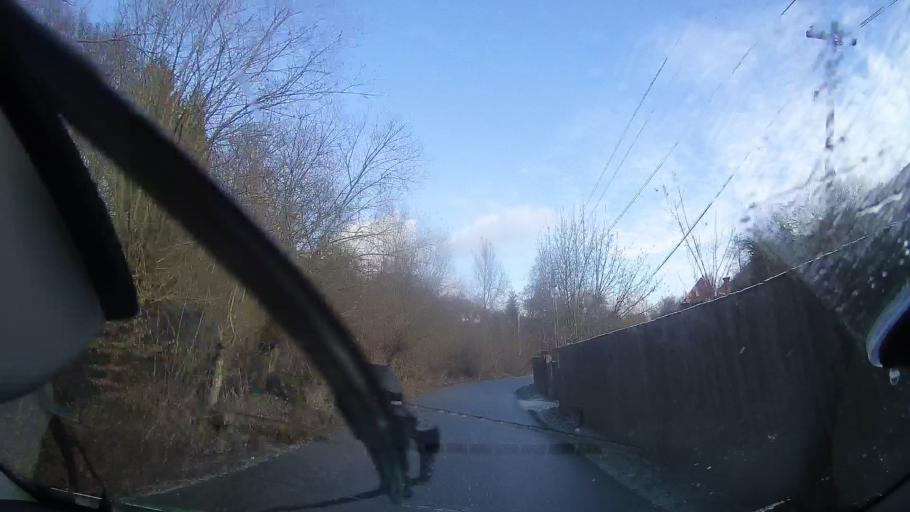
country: RO
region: Alba
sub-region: Comuna Sohodol
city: Sohodol
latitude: 46.3396
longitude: 23.0124
